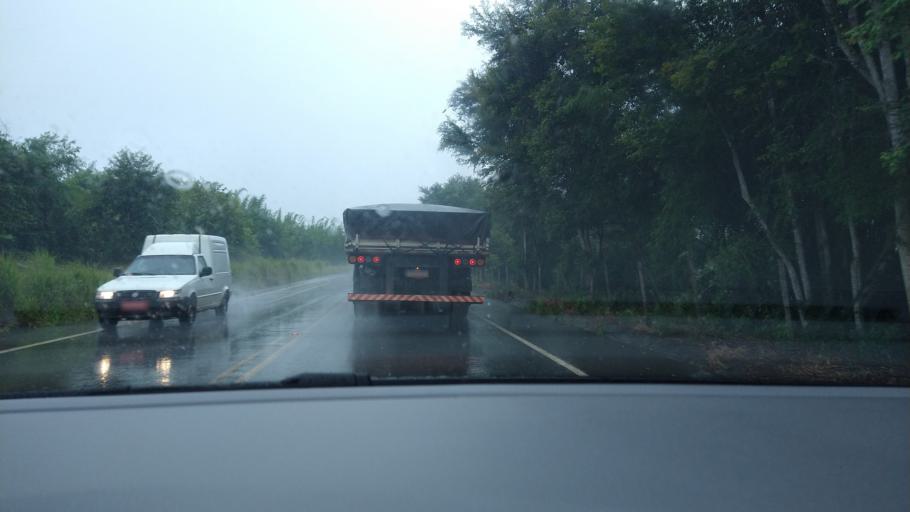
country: BR
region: Minas Gerais
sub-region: Ponte Nova
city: Ponte Nova
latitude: -20.5745
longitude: -42.8755
